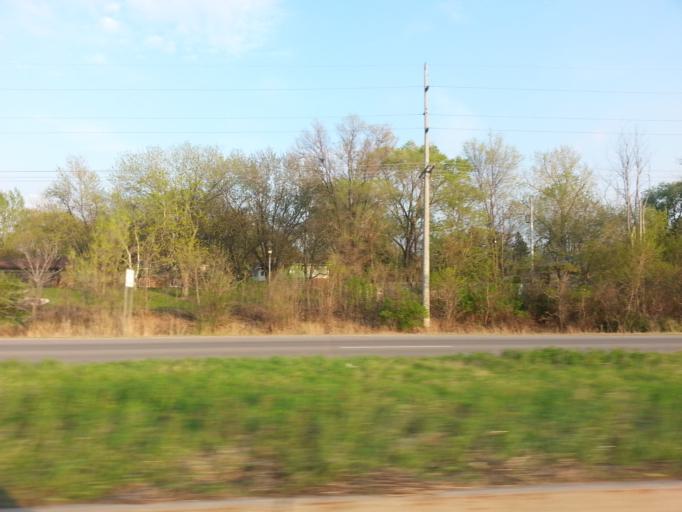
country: US
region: Minnesota
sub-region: Dakota County
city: Burnsville
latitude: 44.7884
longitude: -93.2461
